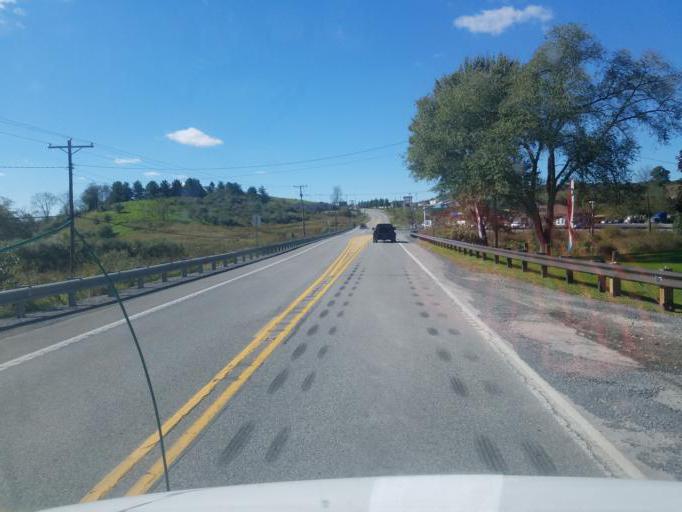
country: US
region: Pennsylvania
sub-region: Bedford County
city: Bedford
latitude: 40.0477
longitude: -78.5487
